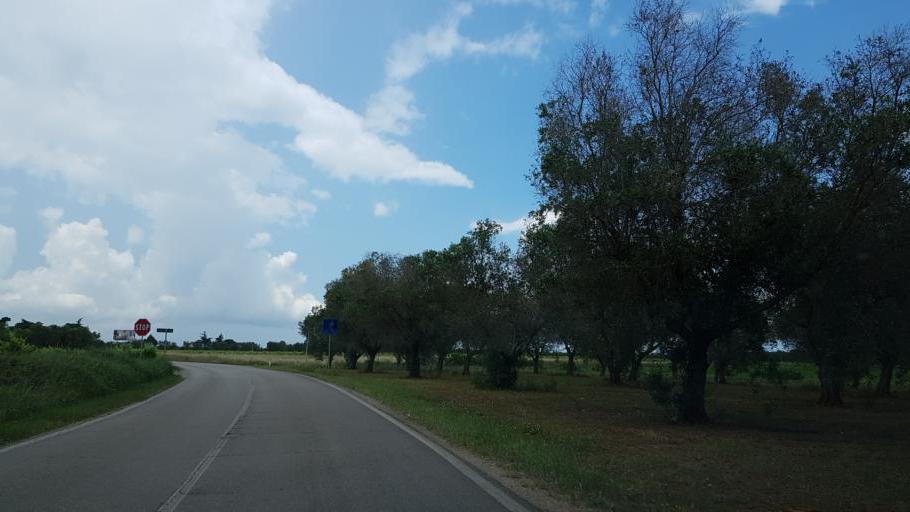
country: IT
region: Apulia
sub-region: Provincia di Brindisi
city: San Donaci
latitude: 40.4667
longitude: 17.9292
